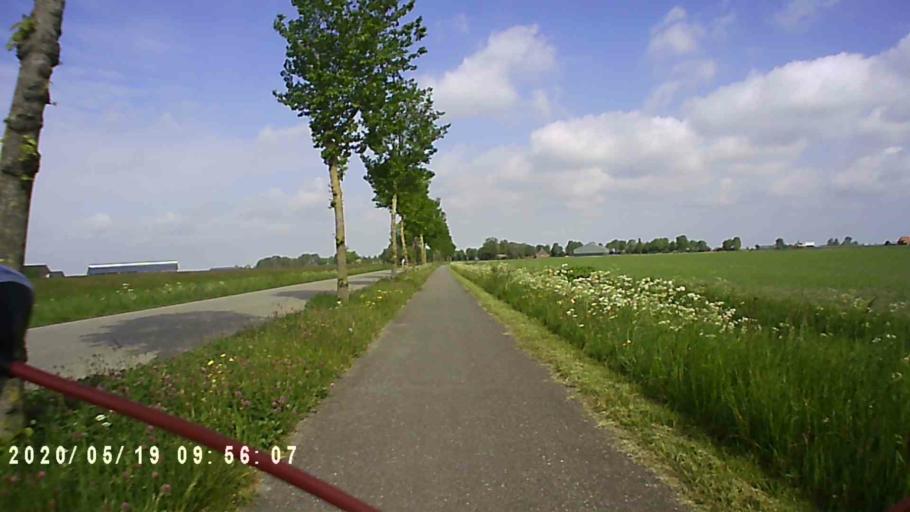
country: NL
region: Groningen
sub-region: Gemeente Zuidhorn
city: Grijpskerk
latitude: 53.2923
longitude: 6.2434
